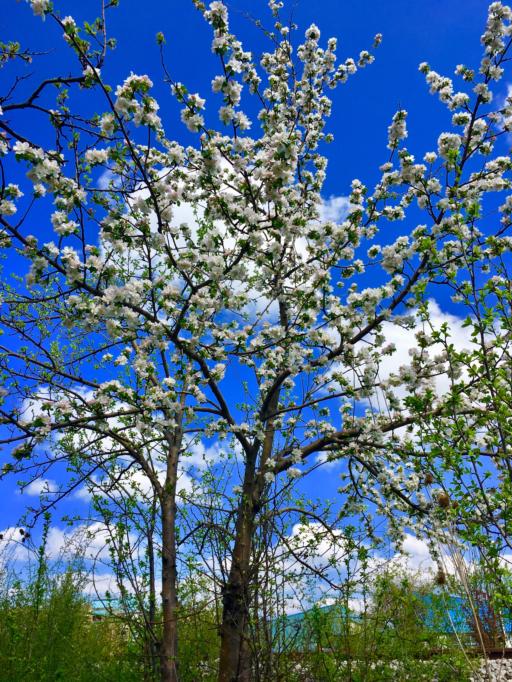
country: XK
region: Pristina
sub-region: Komuna e Drenasit
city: Glogovac
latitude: 42.6411
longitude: 20.9038
